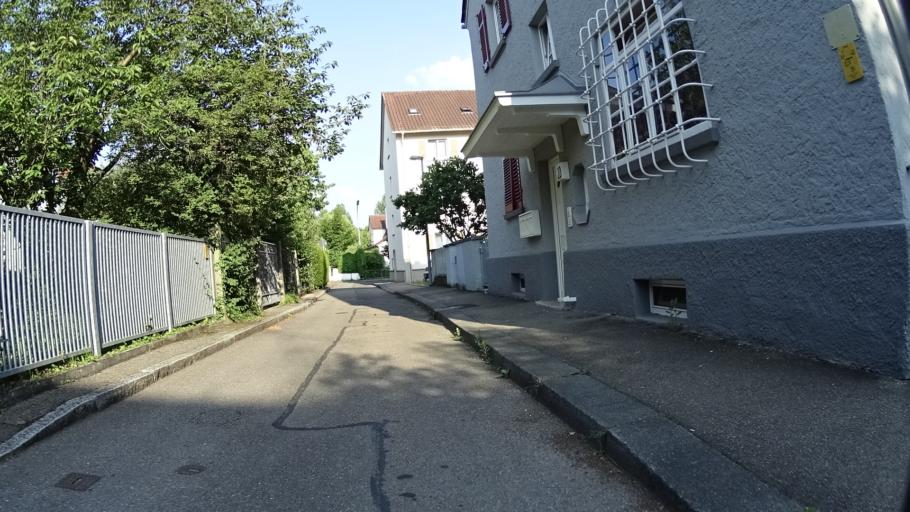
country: DE
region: Baden-Wuerttemberg
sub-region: Regierungsbezirk Stuttgart
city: Goeppingen
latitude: 48.7064
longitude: 9.6638
